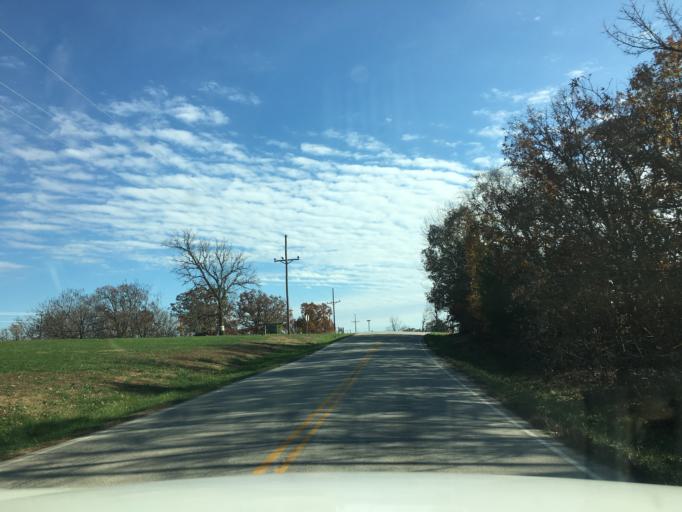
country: US
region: Missouri
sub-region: Maries County
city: Belle
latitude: 38.3560
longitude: -91.8018
